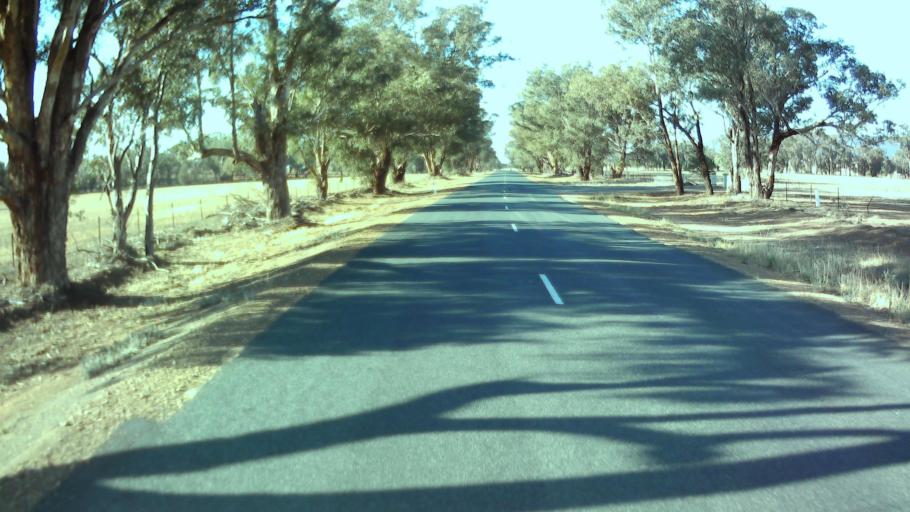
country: AU
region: New South Wales
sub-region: Weddin
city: Grenfell
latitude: -33.9387
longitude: 148.1371
